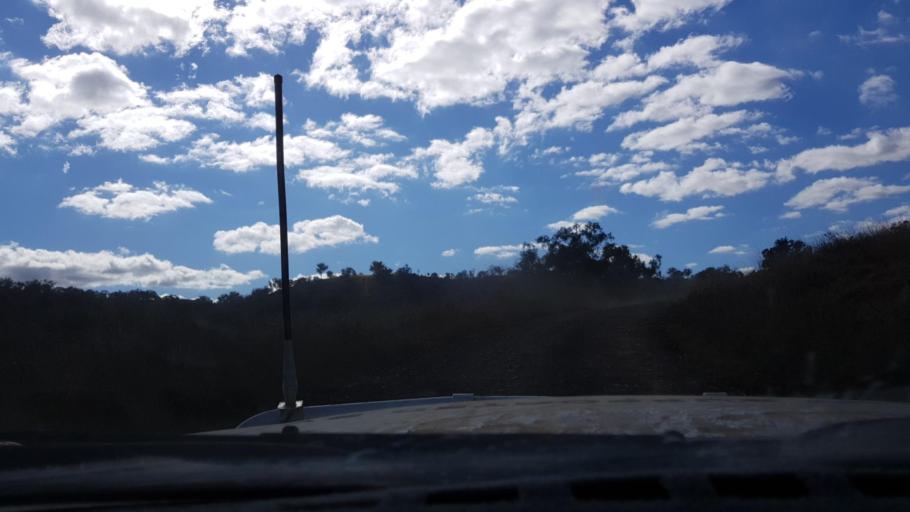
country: AU
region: New South Wales
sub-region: Tamworth Municipality
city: Manilla
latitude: -30.4333
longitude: 150.7912
